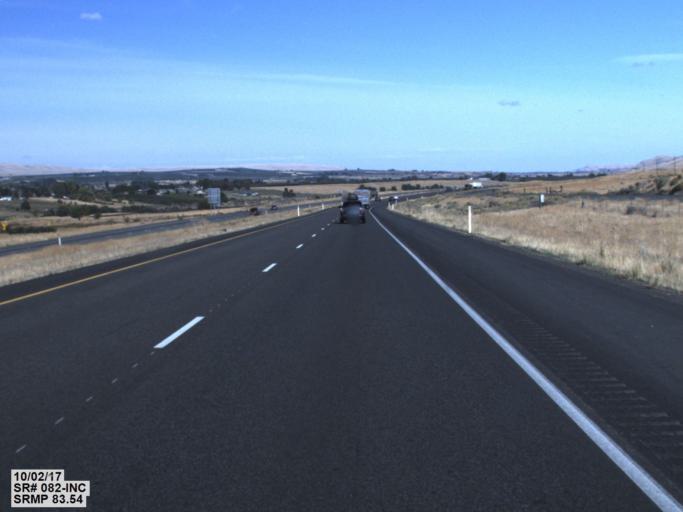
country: US
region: Washington
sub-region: Benton County
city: Prosser
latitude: 46.2156
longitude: -119.7235
